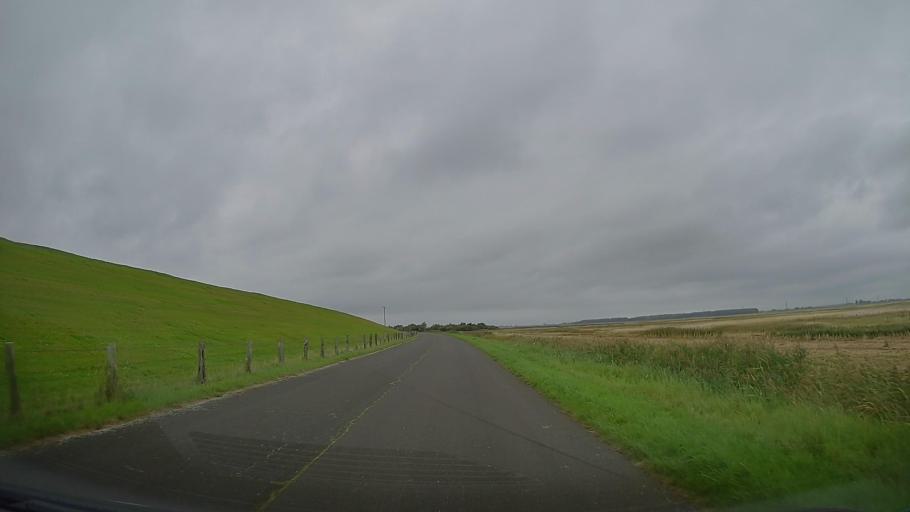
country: DE
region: Schleswig-Holstein
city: Busenwurth
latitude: 54.0440
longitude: 8.9817
